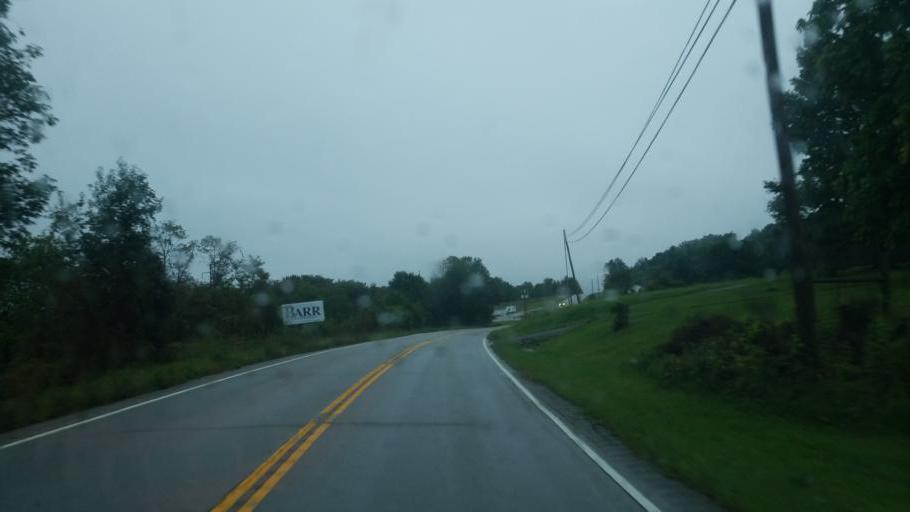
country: US
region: Kentucky
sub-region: Fleming County
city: Flemingsburg
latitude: 38.3839
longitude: -83.6523
